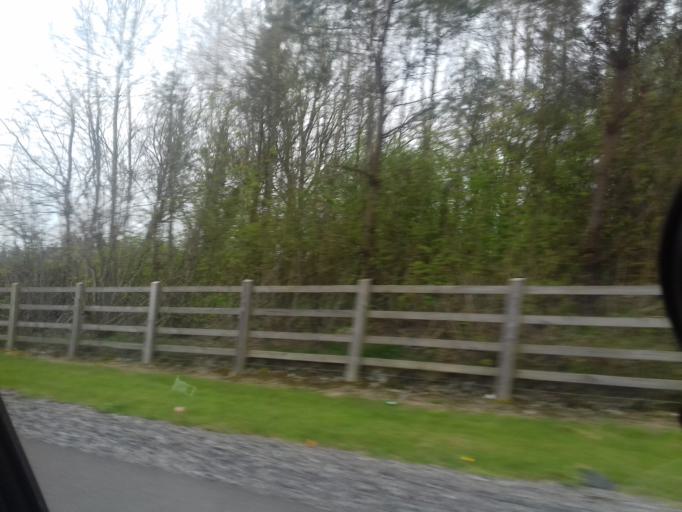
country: IE
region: Leinster
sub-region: An Iarmhi
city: Rochfortbridge
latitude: 53.5073
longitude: -7.2457
